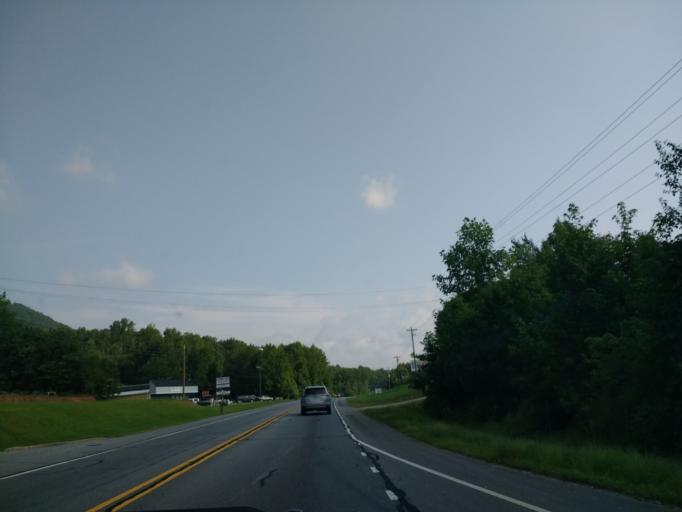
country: US
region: Georgia
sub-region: White County
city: Cleveland
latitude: 34.5603
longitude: -83.7627
